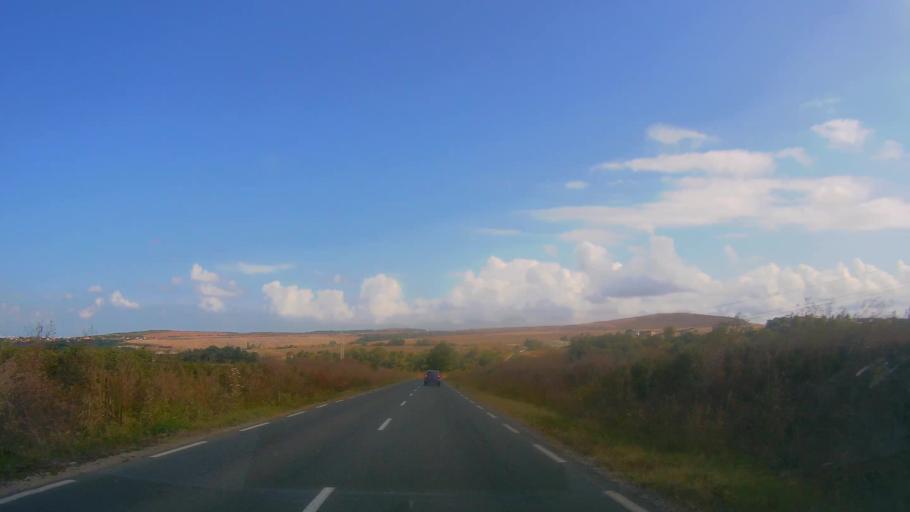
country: BG
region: Burgas
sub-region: Obshtina Kameno
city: Kameno
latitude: 42.4772
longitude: 27.3538
